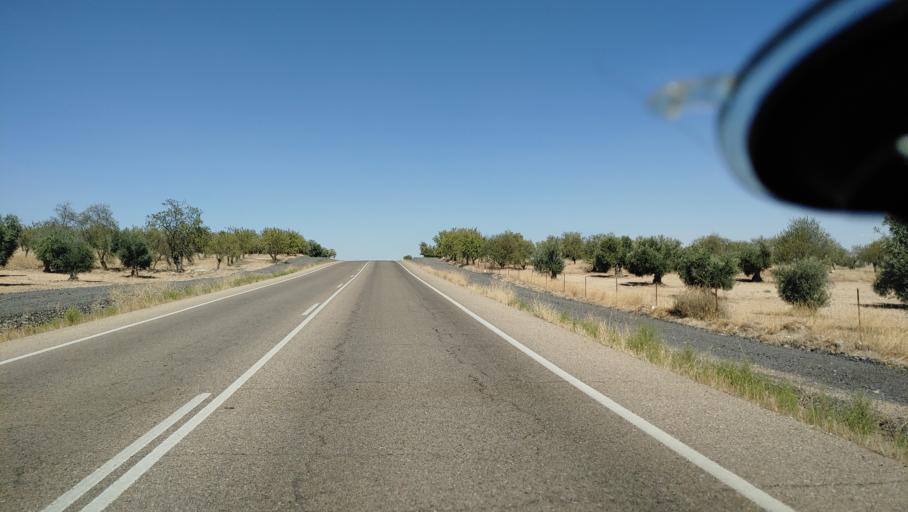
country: ES
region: Castille-La Mancha
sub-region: Province of Toledo
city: Cuerva
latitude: 39.6748
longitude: -4.1873
